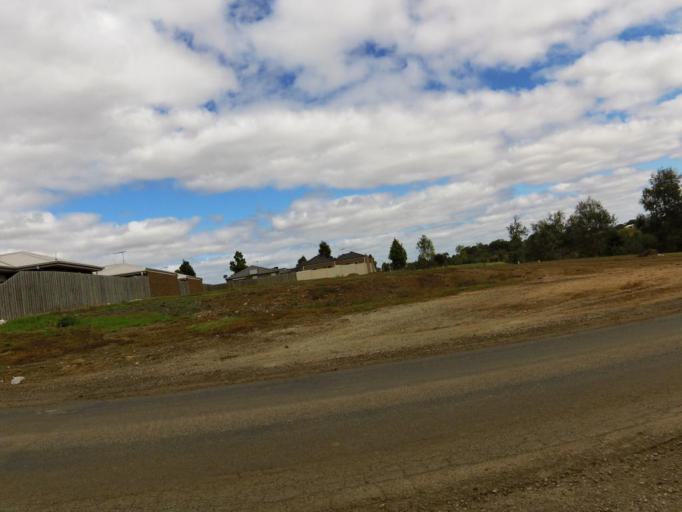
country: AU
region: Victoria
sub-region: Wyndham
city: Tarneit
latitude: -37.8599
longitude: 144.6571
